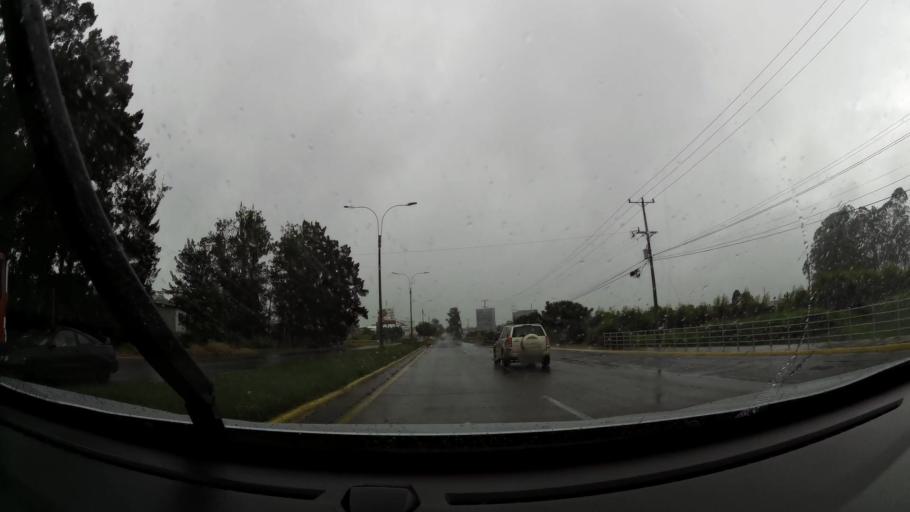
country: CR
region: Cartago
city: Cartago
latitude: 9.8676
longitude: -83.9403
